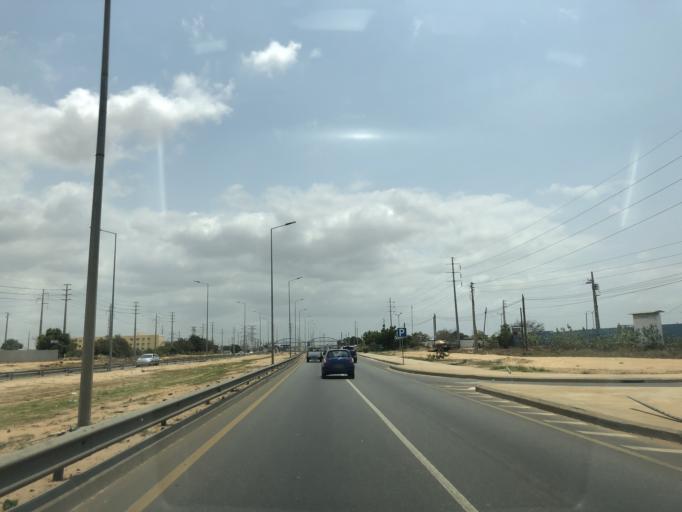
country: AO
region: Luanda
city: Luanda
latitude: -8.9630
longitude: 13.2563
